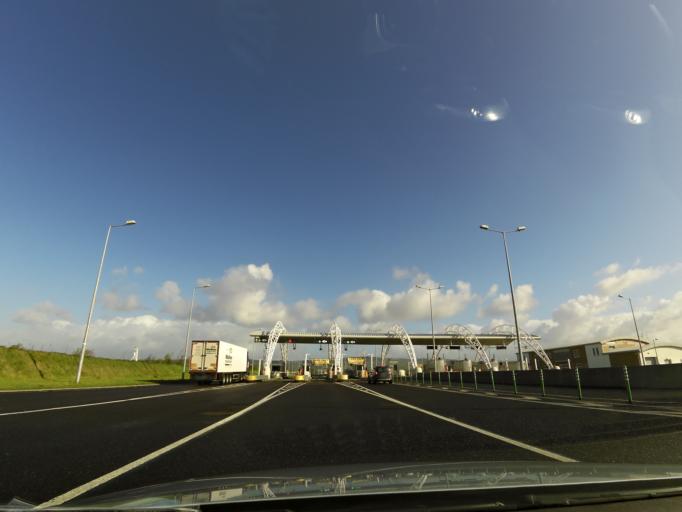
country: IE
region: Munster
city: Moyross
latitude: 52.6689
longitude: -8.7001
